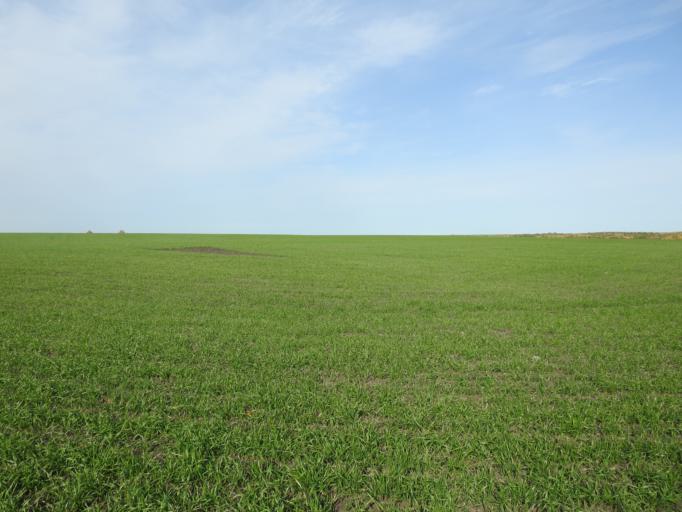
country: RU
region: Saratov
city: Baltay
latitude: 52.5239
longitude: 46.6699
